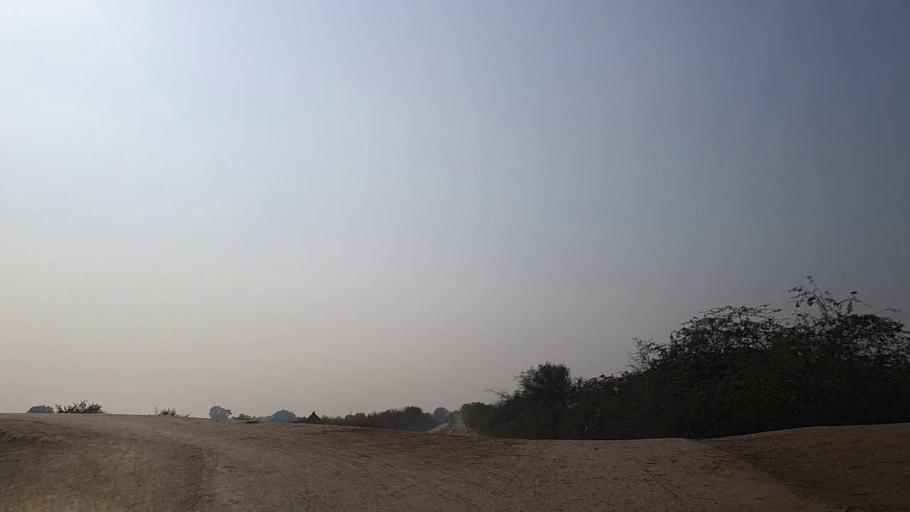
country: PK
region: Sindh
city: Sann
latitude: 26.0996
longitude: 68.1476
